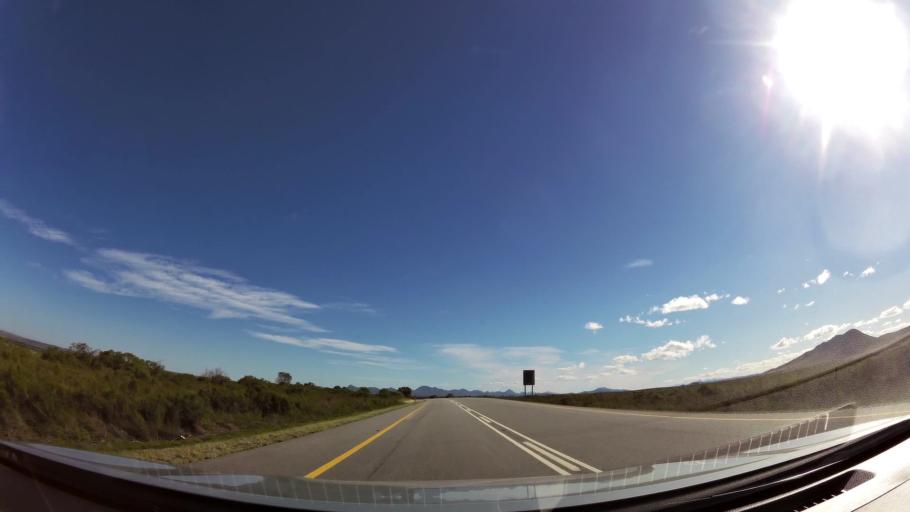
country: ZA
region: Eastern Cape
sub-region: Cacadu District Municipality
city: Kruisfontein
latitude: -34.0100
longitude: 24.6539
